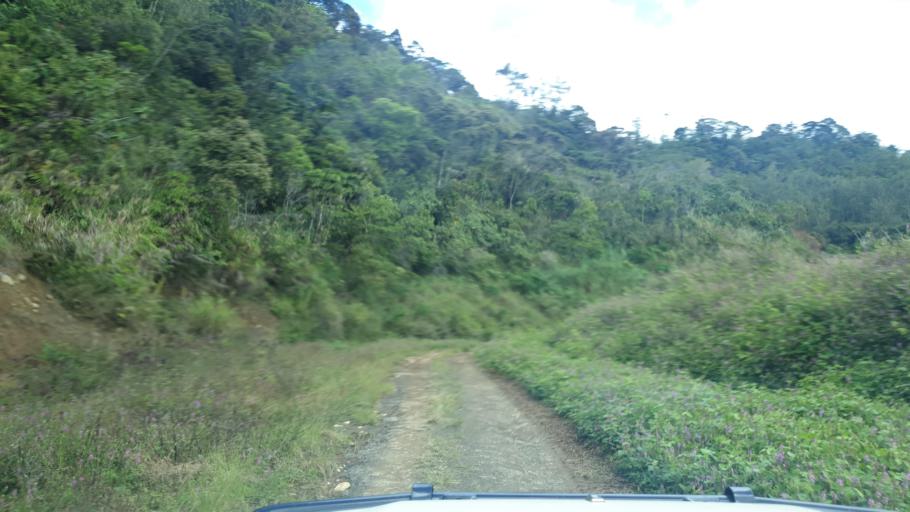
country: PG
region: Eastern Highlands
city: Goroka
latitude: -6.2772
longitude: 145.1891
